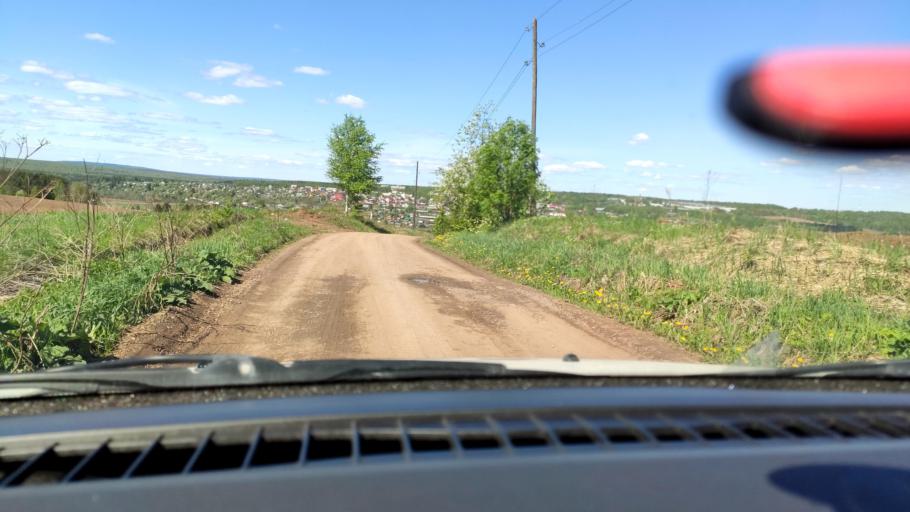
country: RU
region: Perm
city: Bershet'
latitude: 57.7242
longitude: 56.3930
